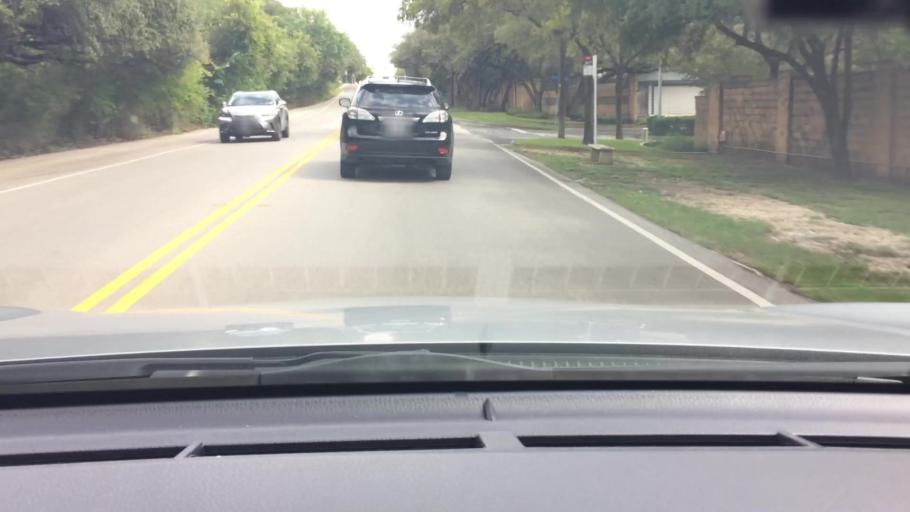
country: US
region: Texas
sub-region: Bexar County
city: Castle Hills
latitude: 29.5460
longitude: -98.5344
